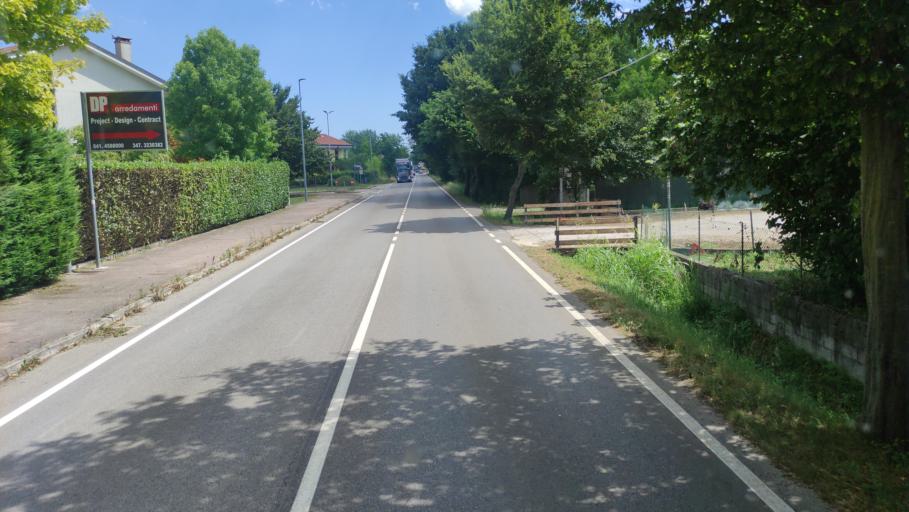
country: IT
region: Veneto
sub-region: Provincia di Venezia
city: Scorze
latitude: 45.5726
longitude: 12.0990
